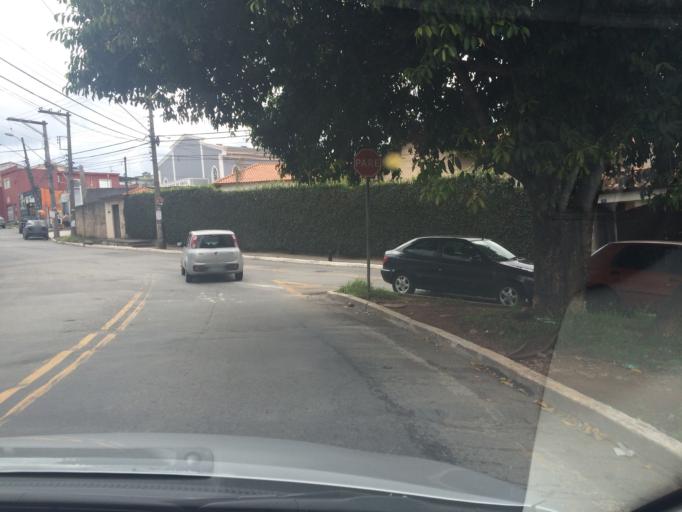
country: BR
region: Sao Paulo
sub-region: Guarulhos
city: Guarulhos
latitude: -23.4309
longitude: -46.5269
